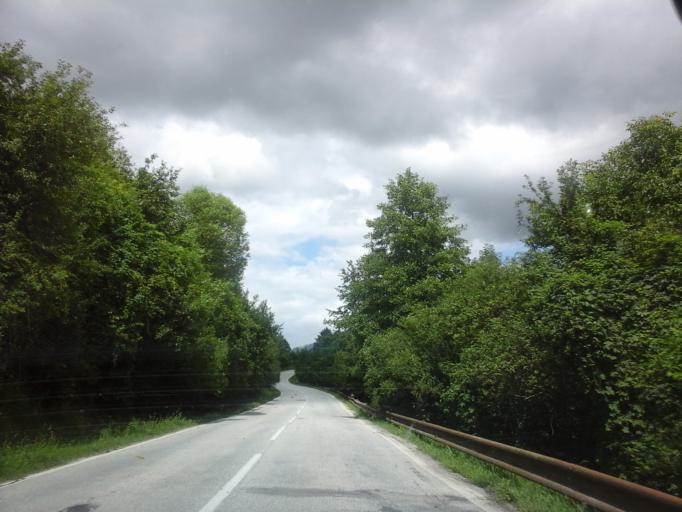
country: SK
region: Kosicky
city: Dobsina
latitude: 48.7296
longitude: 20.4150
